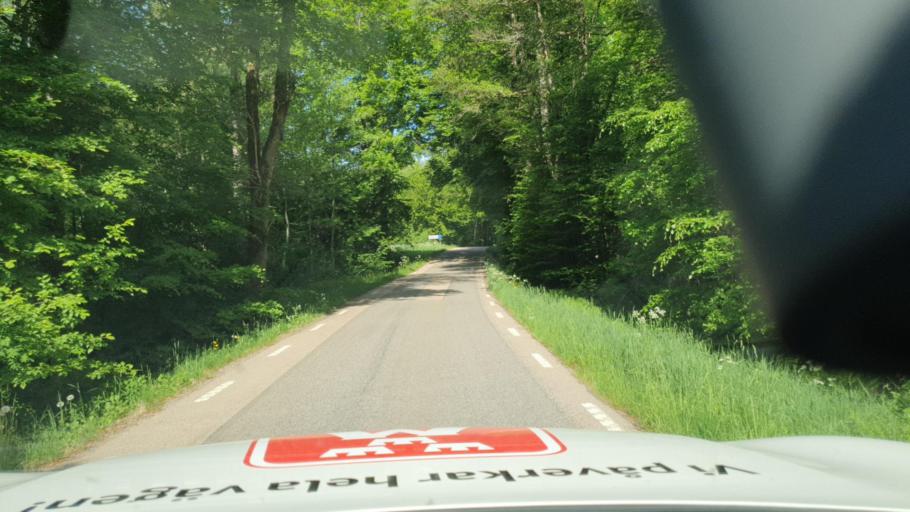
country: SE
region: Vaestra Goetaland
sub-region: Herrljunga Kommun
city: Herrljunga
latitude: 57.9220
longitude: 13.1320
